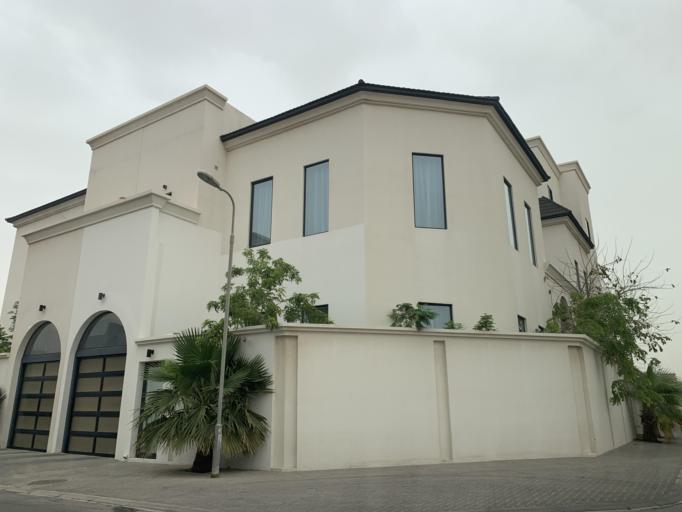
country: BH
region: Northern
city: Ar Rifa'
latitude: 26.1460
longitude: 50.5250
